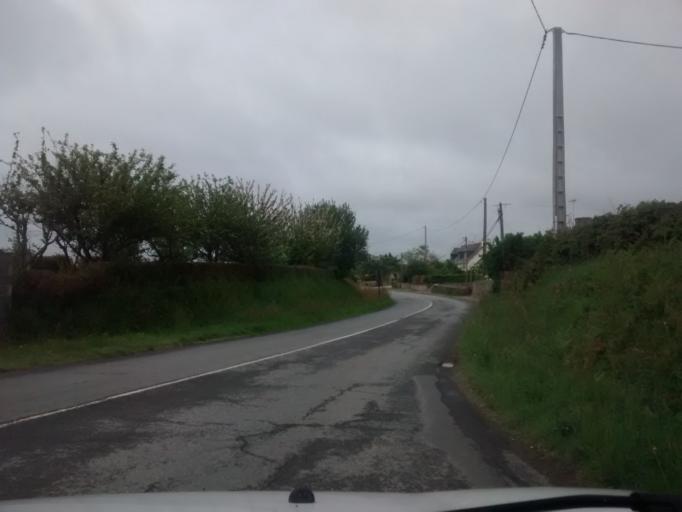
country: FR
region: Brittany
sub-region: Departement des Cotes-d'Armor
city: Plougrescant
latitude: 48.8323
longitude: -3.2354
